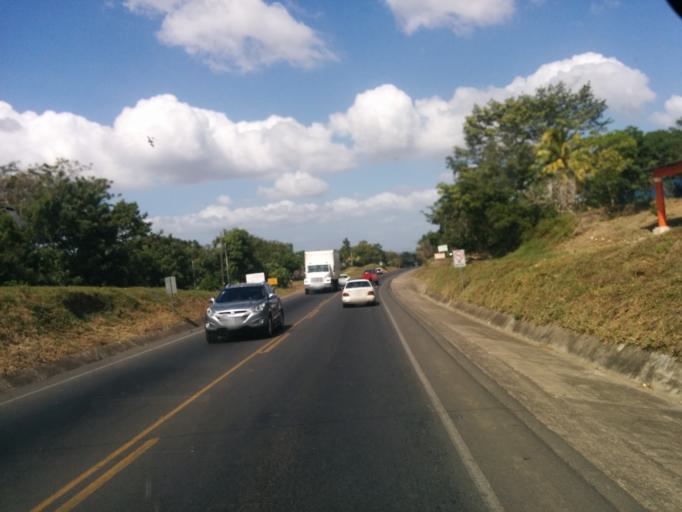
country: NI
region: Masaya
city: Masaya
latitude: 11.9472
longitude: -86.0916
